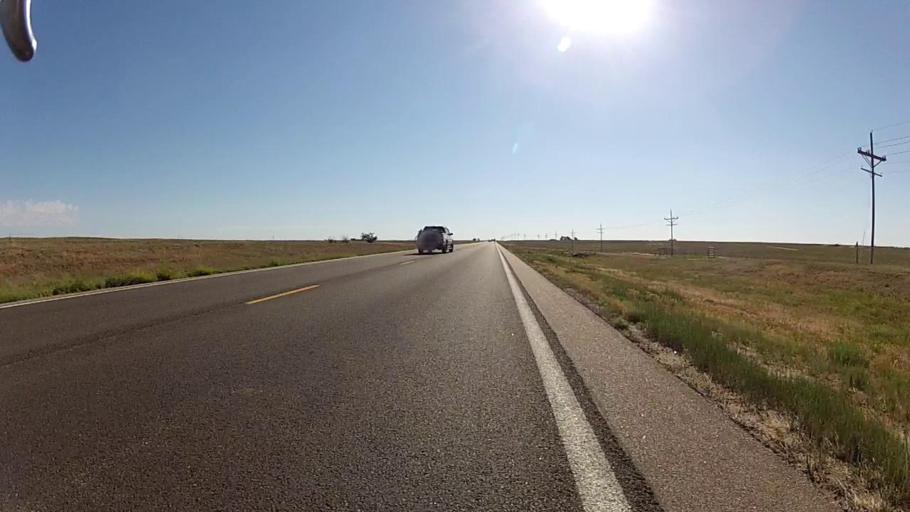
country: US
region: Kansas
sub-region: Haskell County
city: Sublette
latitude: 37.5476
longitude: -100.6119
